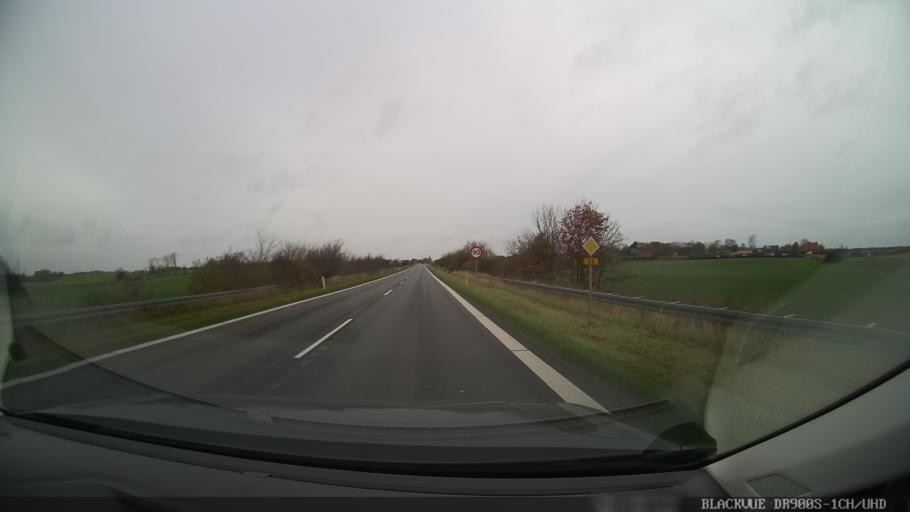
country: DK
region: North Denmark
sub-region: Thisted Kommune
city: Thisted
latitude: 56.8695
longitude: 8.6767
